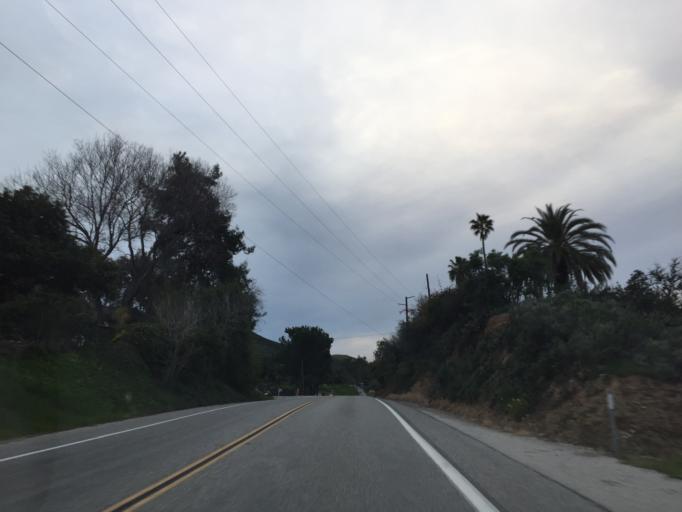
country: US
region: California
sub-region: San Bernardino County
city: Yucaipa
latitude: 34.0748
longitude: -117.0686
